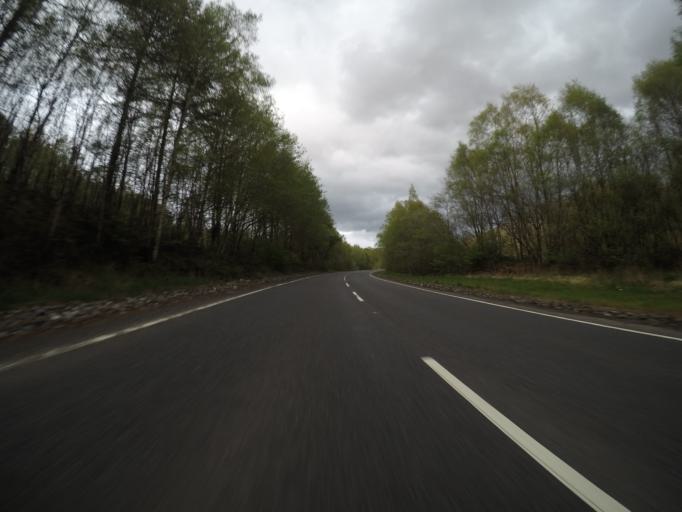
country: GB
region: Scotland
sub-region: Argyll and Bute
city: Garelochhead
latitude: 56.3598
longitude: -4.6771
